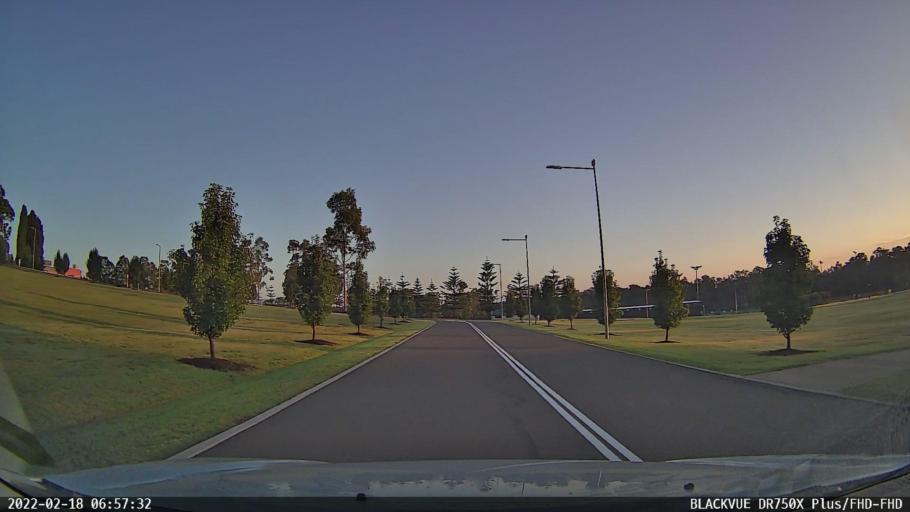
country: AU
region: New South Wales
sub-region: Penrith Municipality
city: Kingswood Park
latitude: -33.7708
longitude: 150.7305
